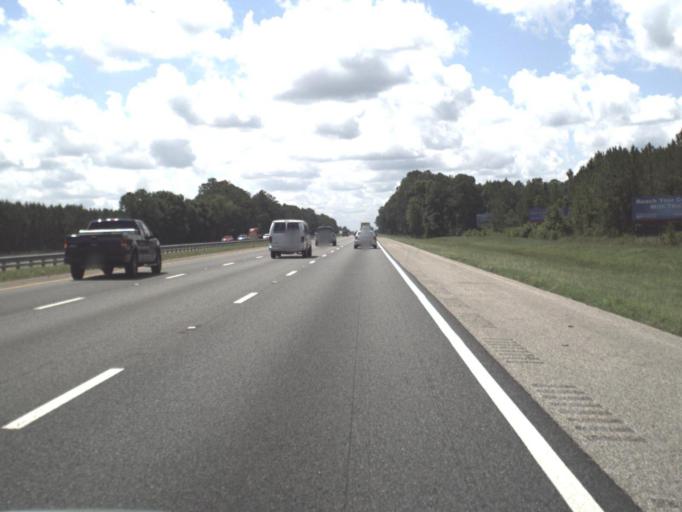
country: US
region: Florida
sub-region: Saint Johns County
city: Saint Augustine Shores
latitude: 29.7815
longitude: -81.3602
